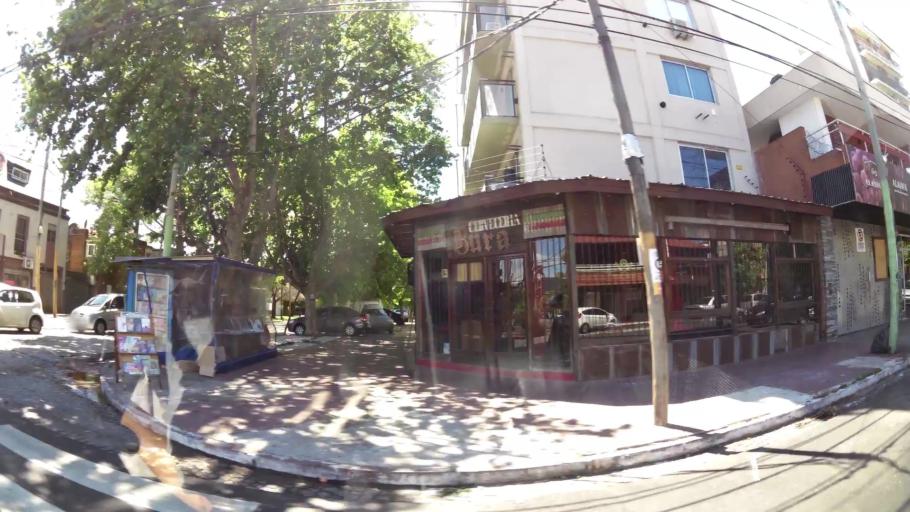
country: AR
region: Buenos Aires
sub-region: Partido de Quilmes
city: Quilmes
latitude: -34.7201
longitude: -58.2680
